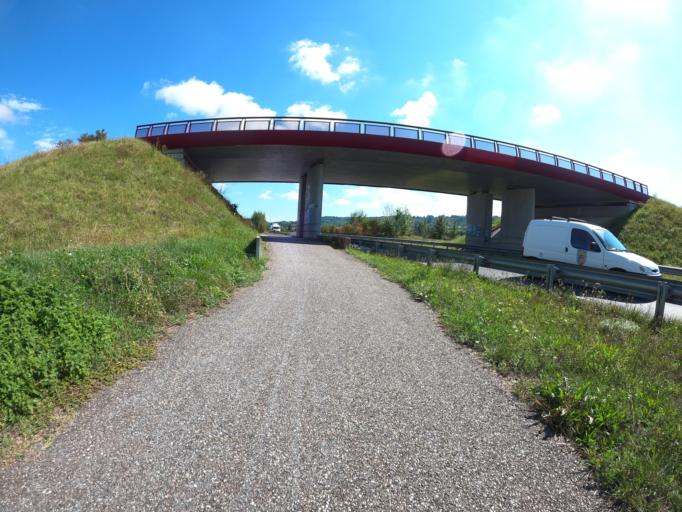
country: FR
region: Aquitaine
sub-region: Departement du Lot-et-Garonne
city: Pujols
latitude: 44.3977
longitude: 0.6806
